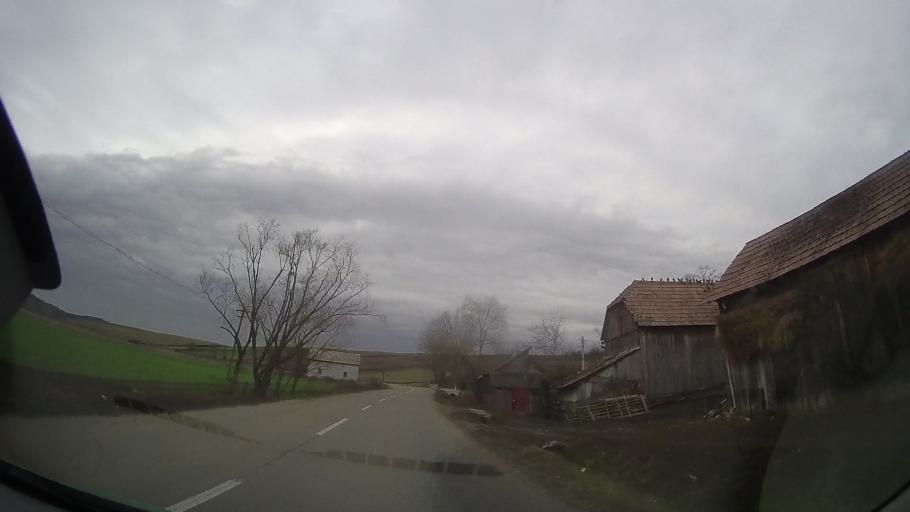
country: RO
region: Bistrita-Nasaud
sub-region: Comuna Milas
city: Milas
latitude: 46.7945
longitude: 24.4219
